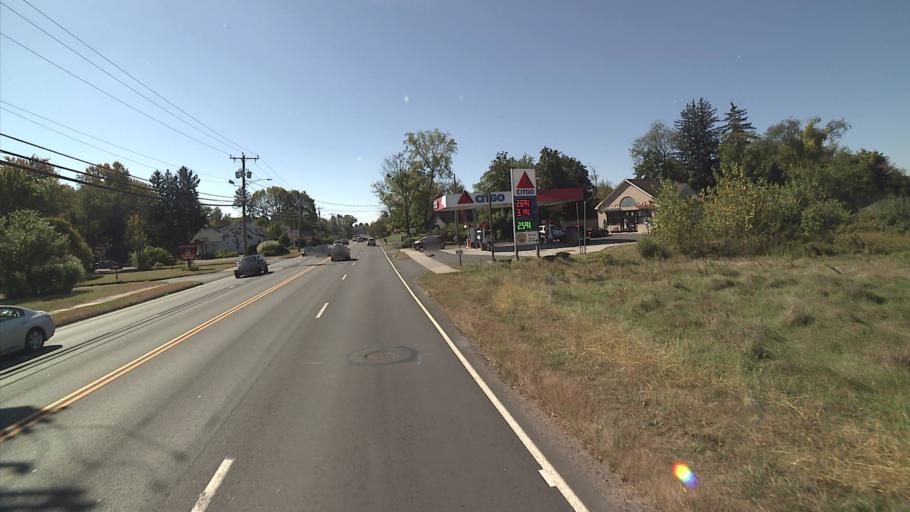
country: US
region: Connecticut
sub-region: Tolland County
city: Rockville
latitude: 41.8361
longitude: -72.4919
